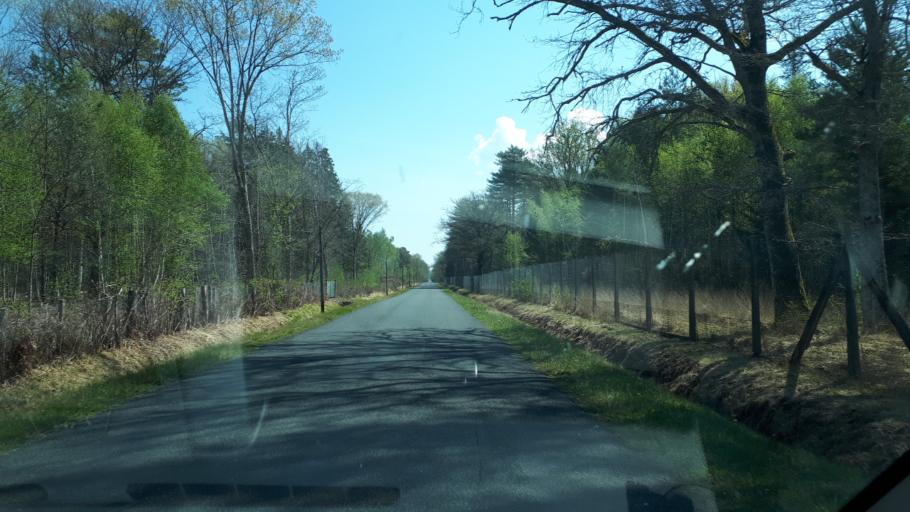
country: FR
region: Centre
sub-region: Departement du Cher
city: Neuvy-sur-Barangeon
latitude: 47.3179
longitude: 2.2247
